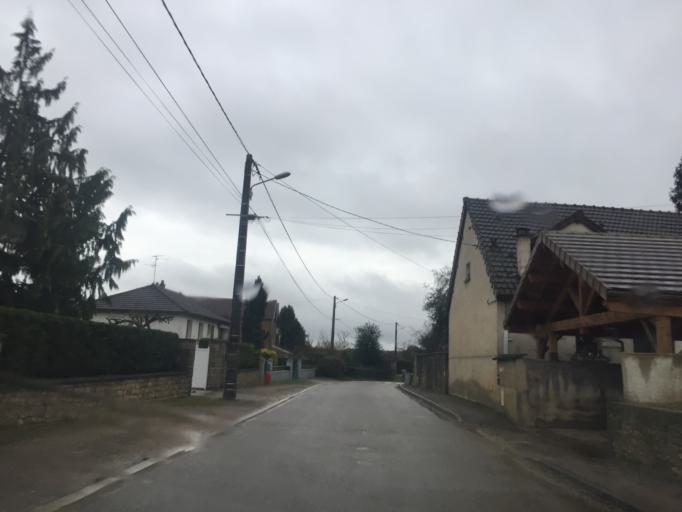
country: FR
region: Franche-Comte
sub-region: Departement du Jura
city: Dole
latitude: 47.0986
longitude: 5.5239
